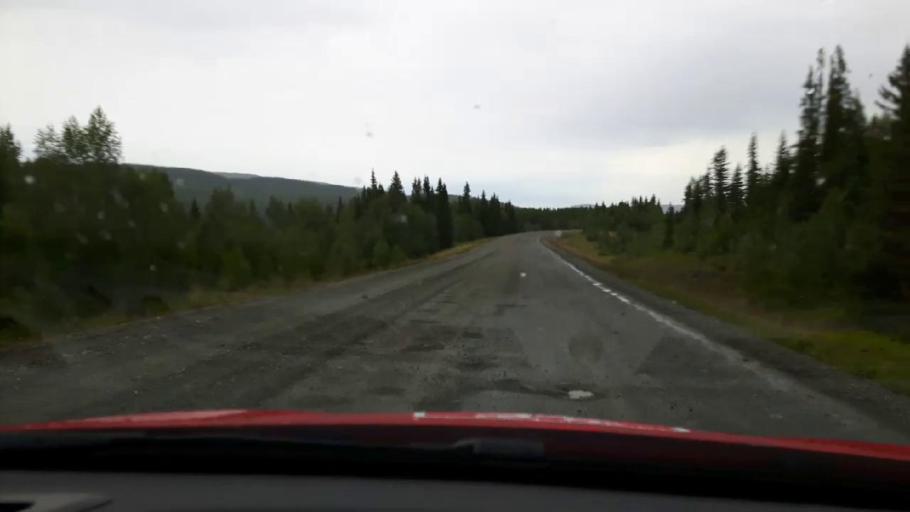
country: SE
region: Jaemtland
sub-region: Are Kommun
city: Are
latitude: 63.4114
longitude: 12.7873
